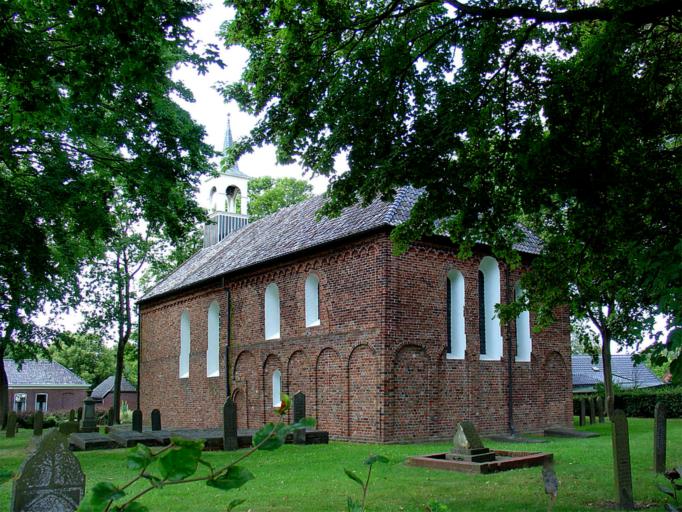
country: NL
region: Friesland
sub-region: Gemeente Leeuwarden
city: Wirdum
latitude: 53.1500
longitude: 5.8041
